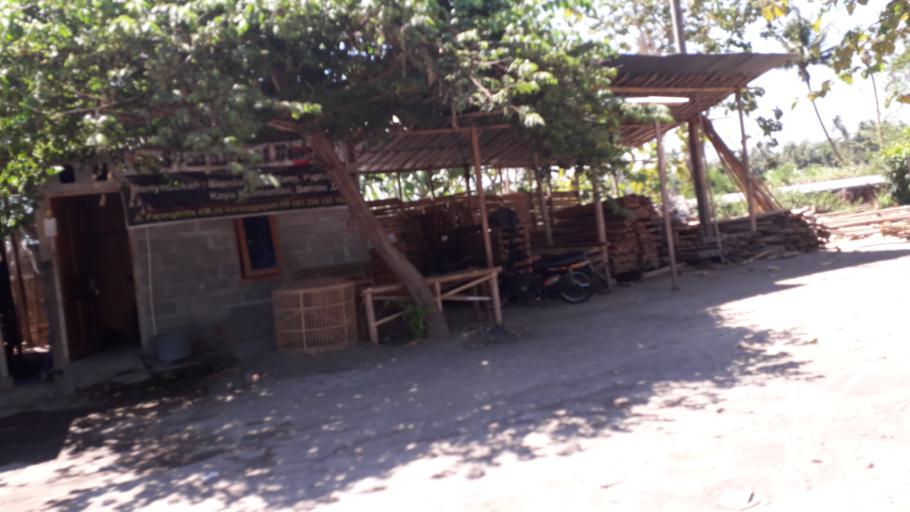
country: ID
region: Daerah Istimewa Yogyakarta
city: Pundong
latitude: -7.9613
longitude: 110.3221
